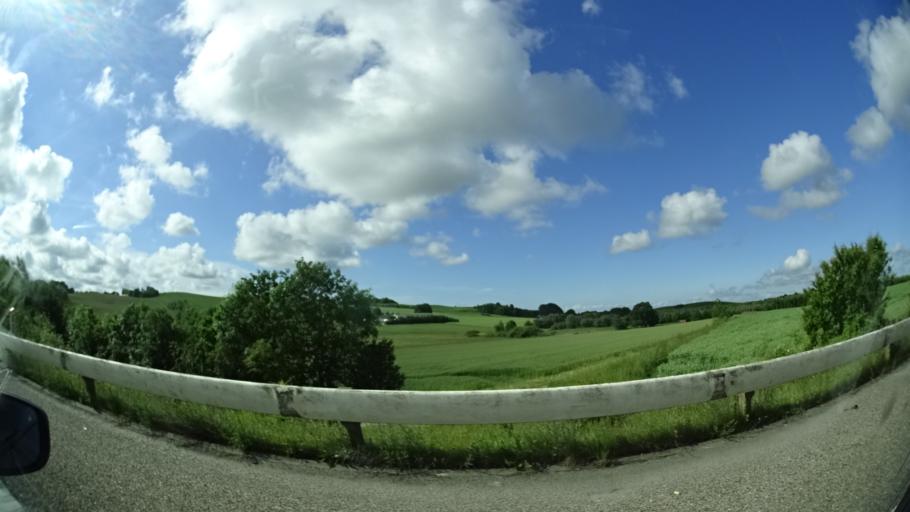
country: DK
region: Central Jutland
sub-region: Syddjurs Kommune
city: Ronde
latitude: 56.3170
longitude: 10.4803
